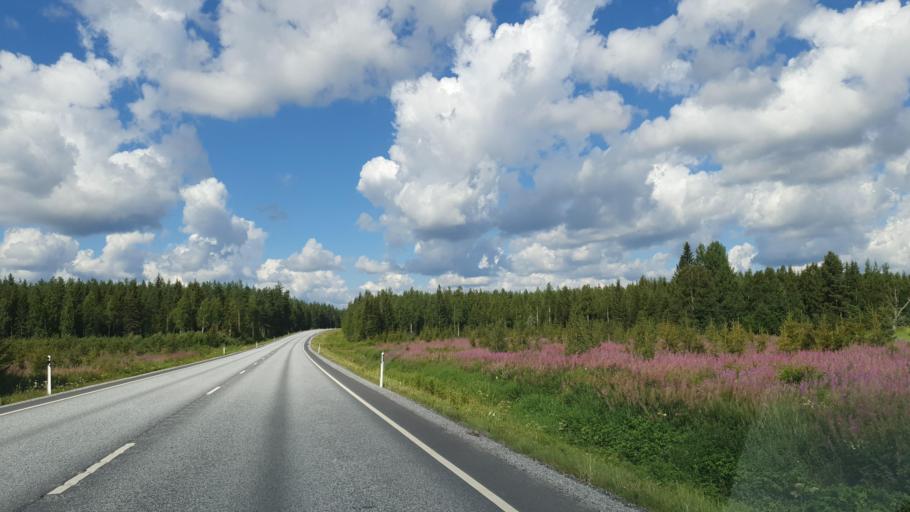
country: FI
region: Northern Savo
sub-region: Ylae-Savo
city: Sonkajaervi
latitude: 63.8994
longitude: 27.3998
